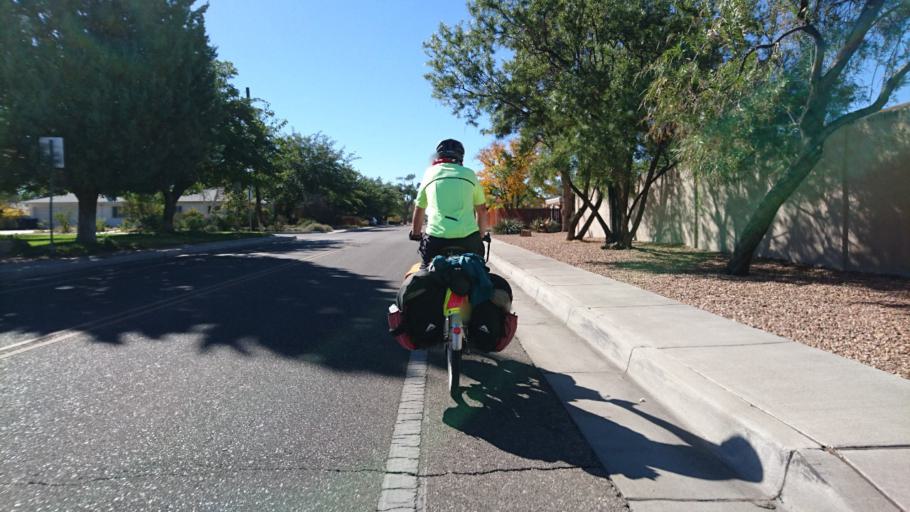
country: US
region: New Mexico
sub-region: Bernalillo County
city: Albuquerque
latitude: 35.0841
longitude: -106.5954
